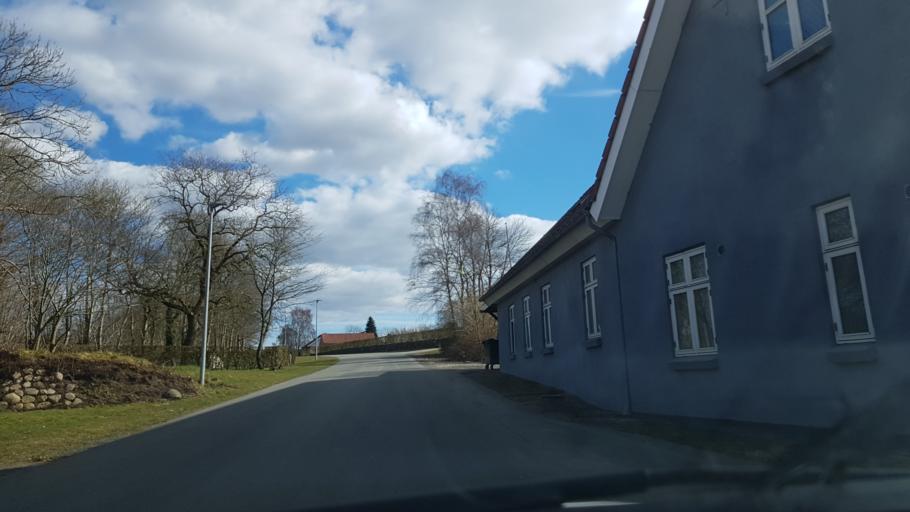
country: DK
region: South Denmark
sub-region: Kolding Kommune
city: Vamdrup
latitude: 55.3565
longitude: 9.3595
